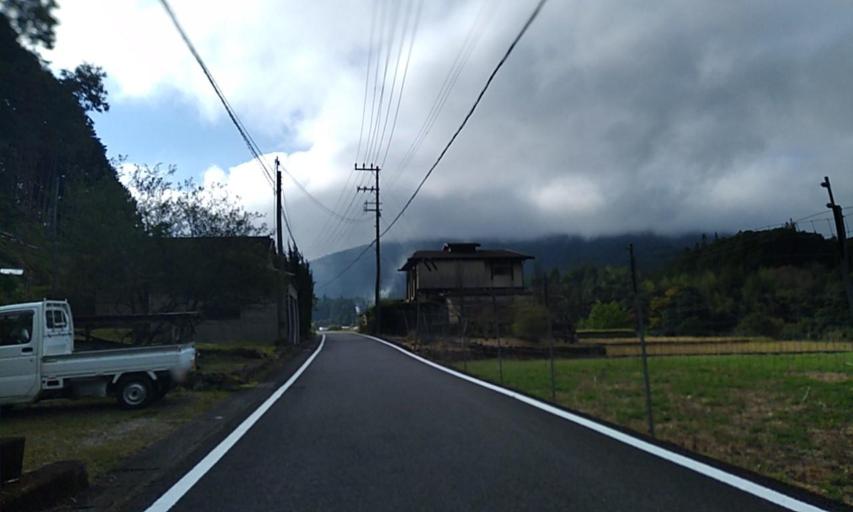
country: JP
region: Wakayama
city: Shingu
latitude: 33.9290
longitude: 135.9795
